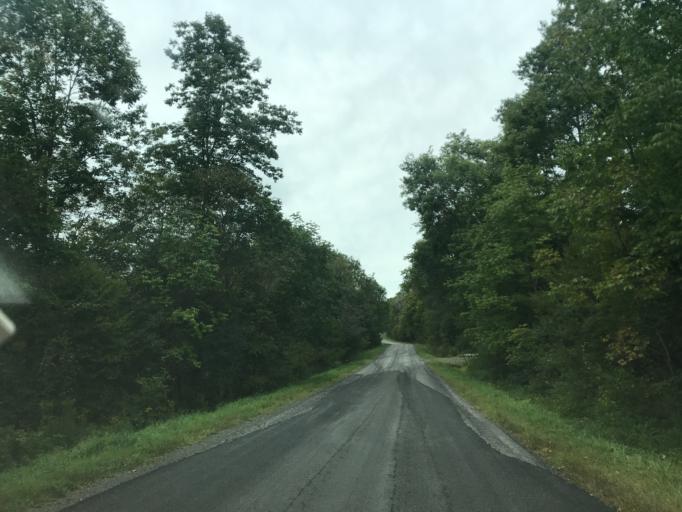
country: US
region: New York
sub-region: Delaware County
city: Stamford
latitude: 42.5132
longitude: -74.6597
